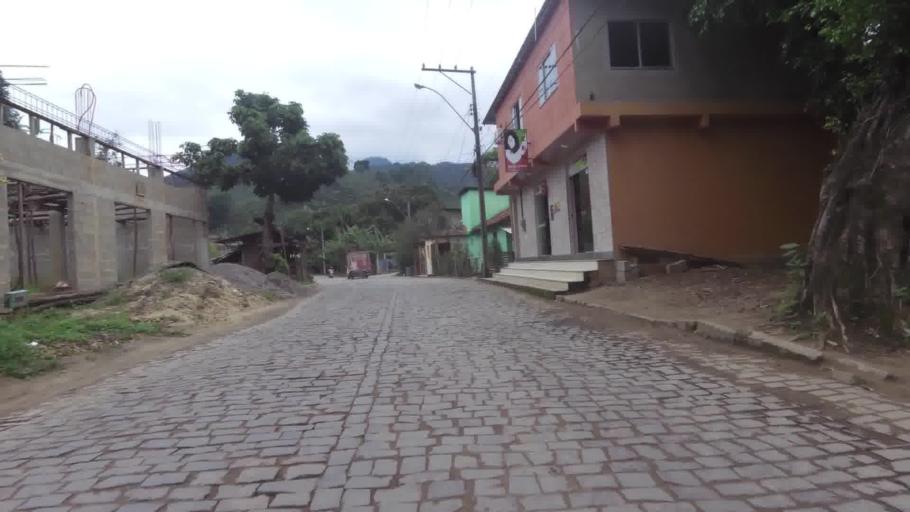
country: BR
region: Espirito Santo
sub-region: Iconha
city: Iconha
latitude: -20.7651
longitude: -40.8331
